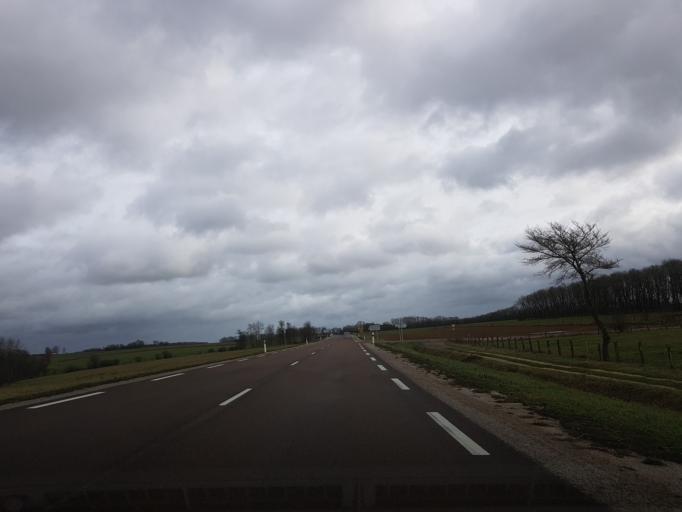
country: FR
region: Champagne-Ardenne
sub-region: Departement de la Haute-Marne
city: Chalindrey
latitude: 47.8457
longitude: 5.4462
